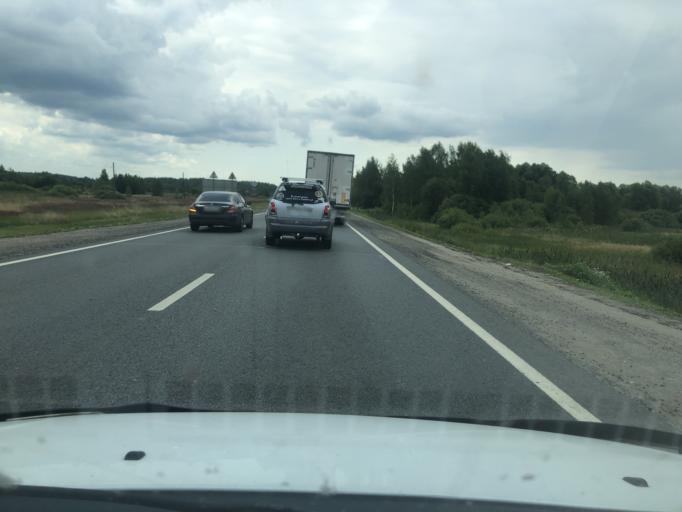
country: RU
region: Jaroslavl
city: Pereslavl'-Zalesskiy
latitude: 56.7812
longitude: 38.8850
